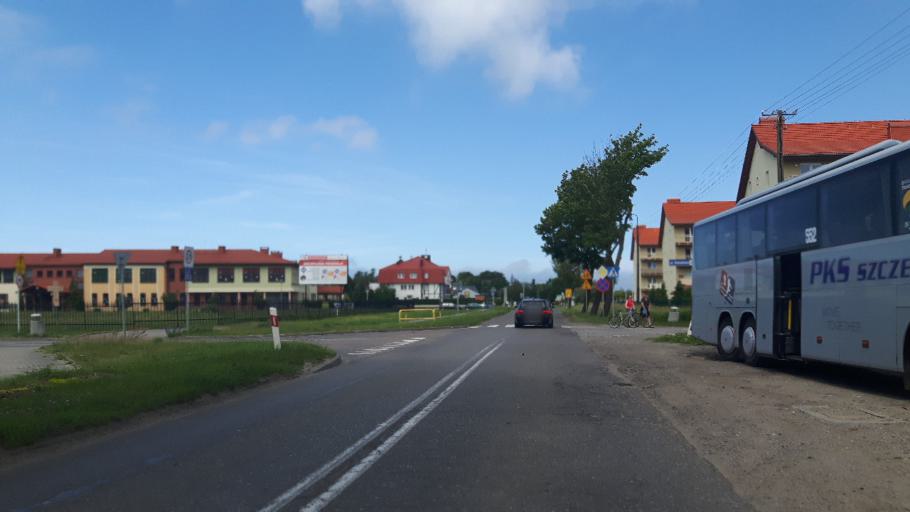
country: PL
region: Pomeranian Voivodeship
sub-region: Powiat slupski
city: Ustka
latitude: 54.5721
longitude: 16.8515
